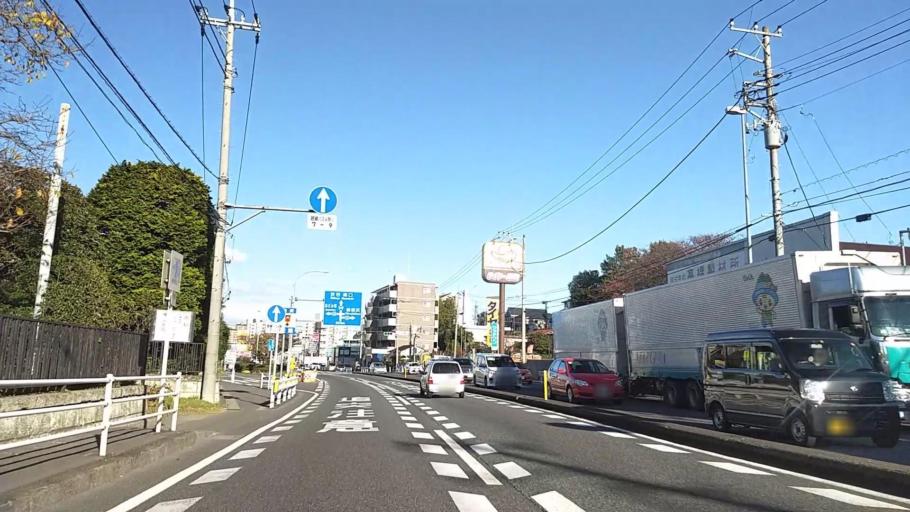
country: JP
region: Tokyo
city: Chofugaoka
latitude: 35.5592
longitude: 139.5553
